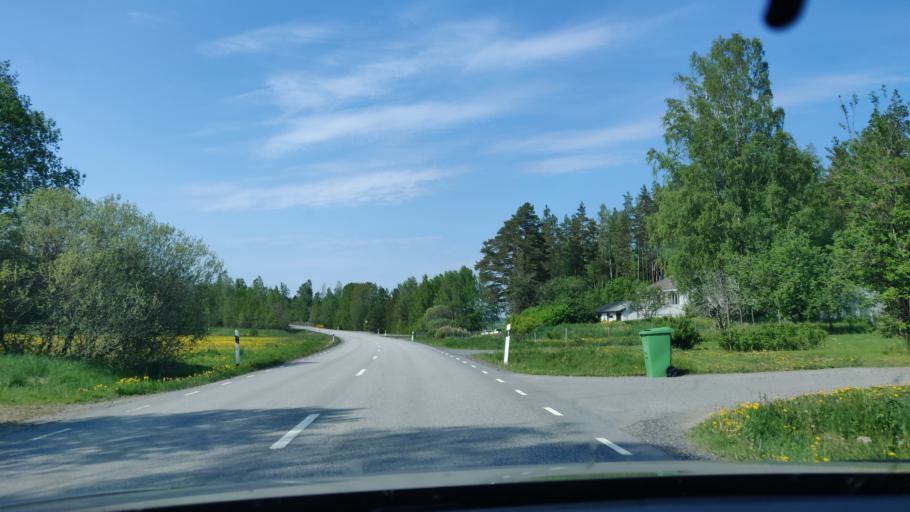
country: SE
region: Uppsala
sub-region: Heby Kommun
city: OEstervala
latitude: 60.1385
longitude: 17.2165
